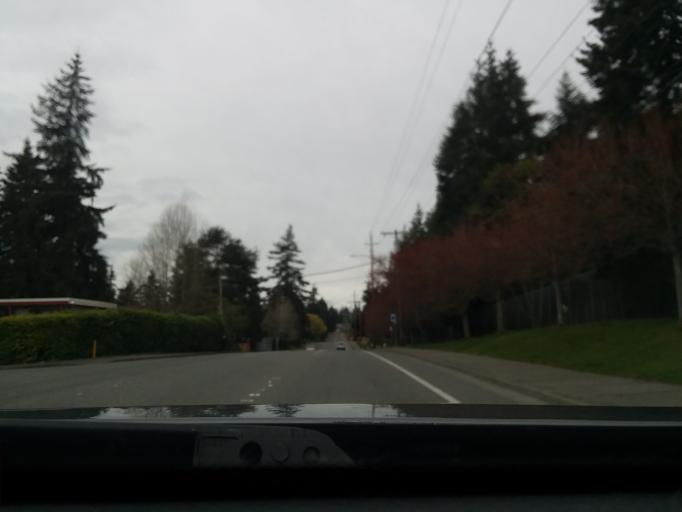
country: US
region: Washington
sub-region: Snohomish County
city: Lynnwood
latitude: 47.8106
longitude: -122.3272
